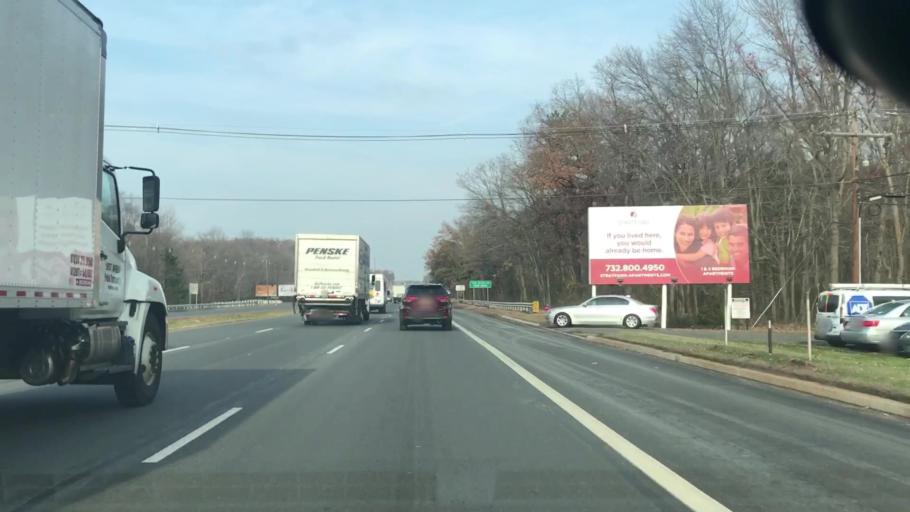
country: US
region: New Jersey
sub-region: Middlesex County
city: Brownville
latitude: 40.4128
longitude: -74.3052
